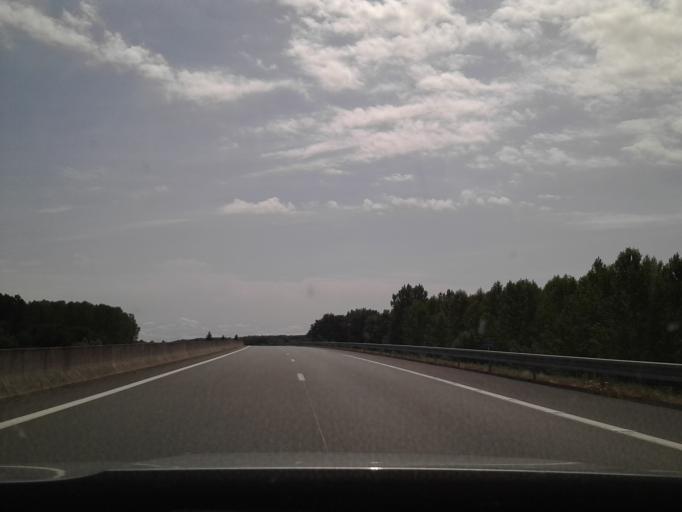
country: FR
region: Pays de la Loire
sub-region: Departement de la Sarthe
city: Chateau-du-Loir
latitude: 47.6628
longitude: 0.3820
